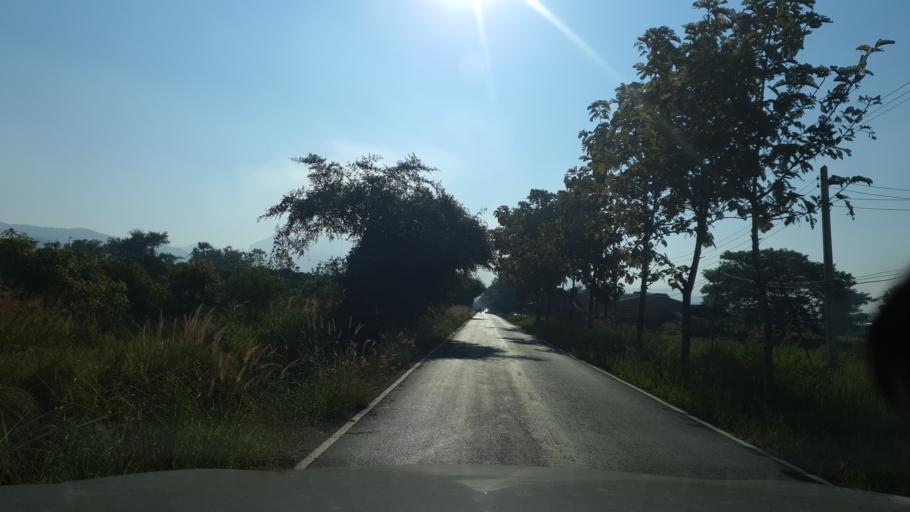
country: TH
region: Chiang Mai
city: San Kamphaeng
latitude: 18.6957
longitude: 99.1504
